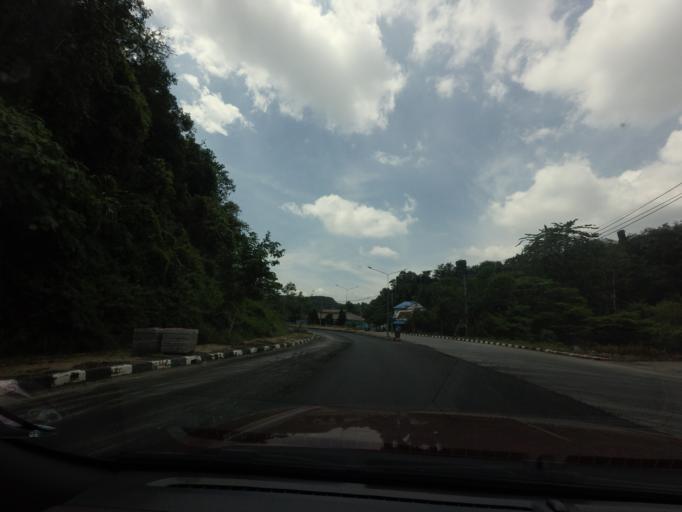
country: TH
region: Yala
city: Betong
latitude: 5.7675
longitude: 101.0559
